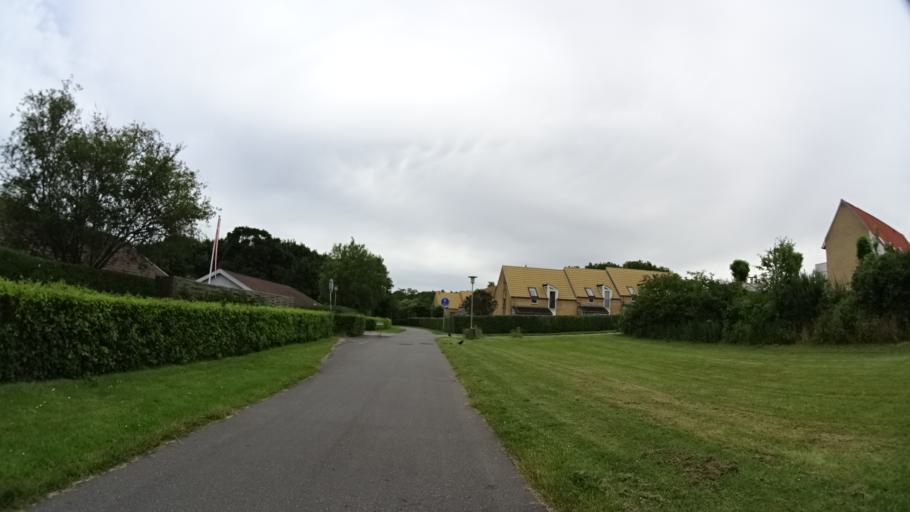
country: DK
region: Central Jutland
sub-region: Arhus Kommune
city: Stavtrup
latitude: 56.1247
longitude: 10.1315
